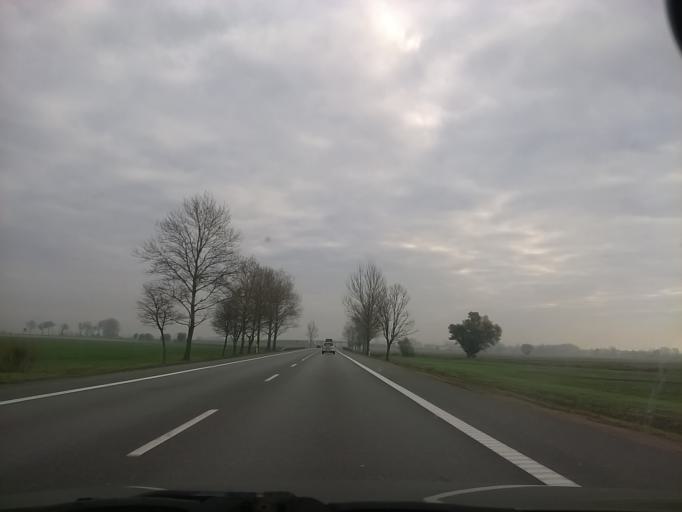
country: PL
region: Pomeranian Voivodeship
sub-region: Powiat nowodworski
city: Nowy Dwor Gdanski
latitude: 54.1968
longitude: 19.1285
